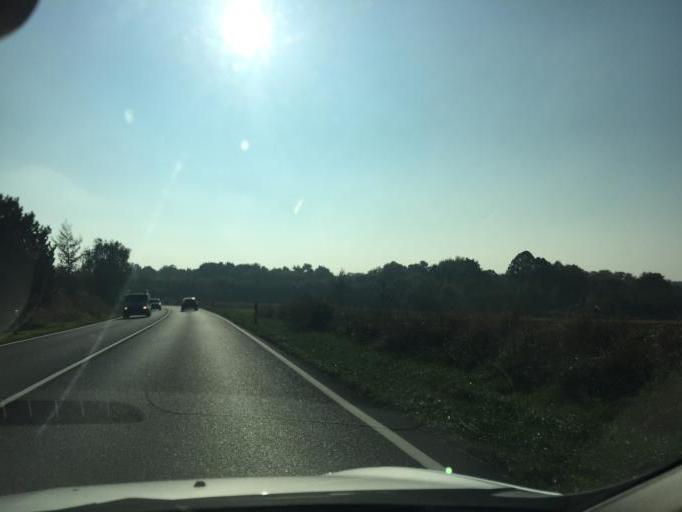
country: LU
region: Luxembourg
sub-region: Canton de Luxembourg
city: Sandweiler
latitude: 49.6122
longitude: 6.2024
